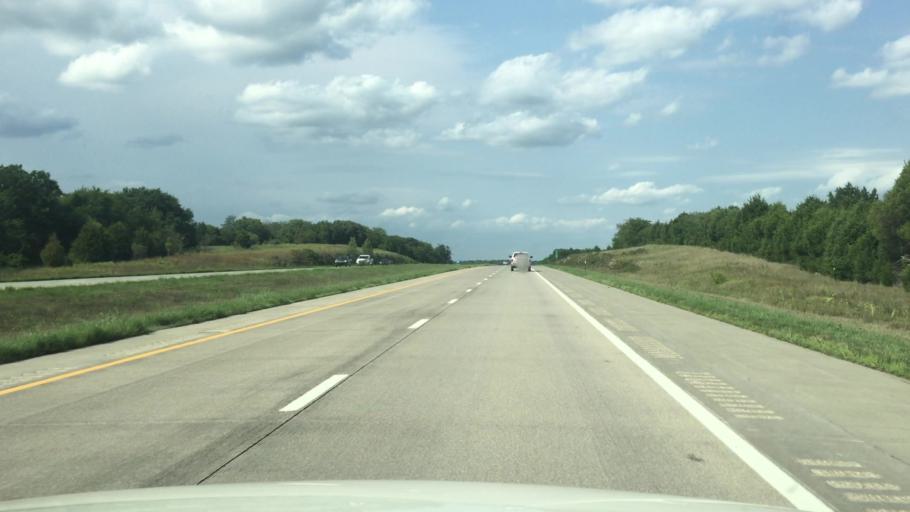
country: US
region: Kansas
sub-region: Miami County
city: Louisburg
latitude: 38.5816
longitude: -94.6951
